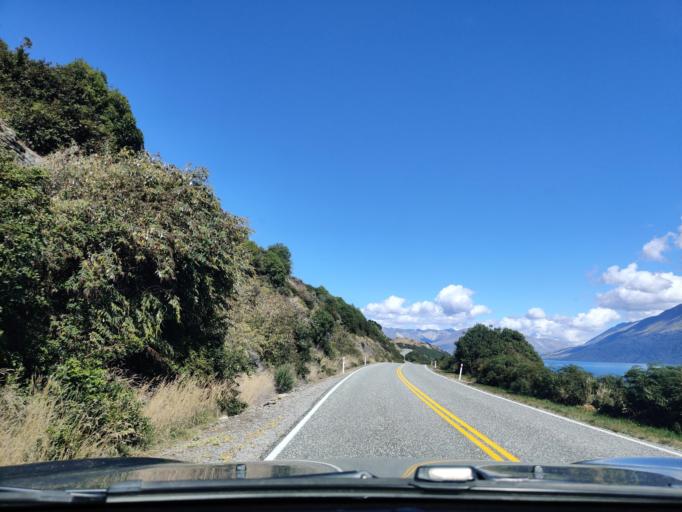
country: NZ
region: Otago
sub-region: Queenstown-Lakes District
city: Queenstown
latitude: -44.9563
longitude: 168.4381
